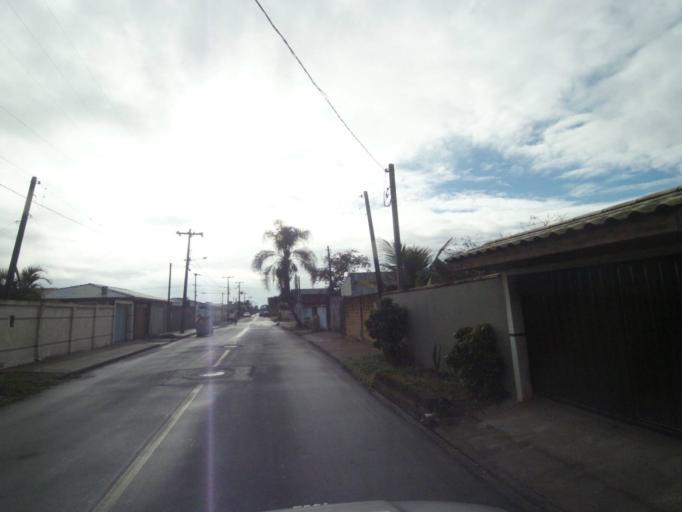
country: BR
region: Parana
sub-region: Paranagua
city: Paranagua
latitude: -25.5644
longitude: -48.5689
